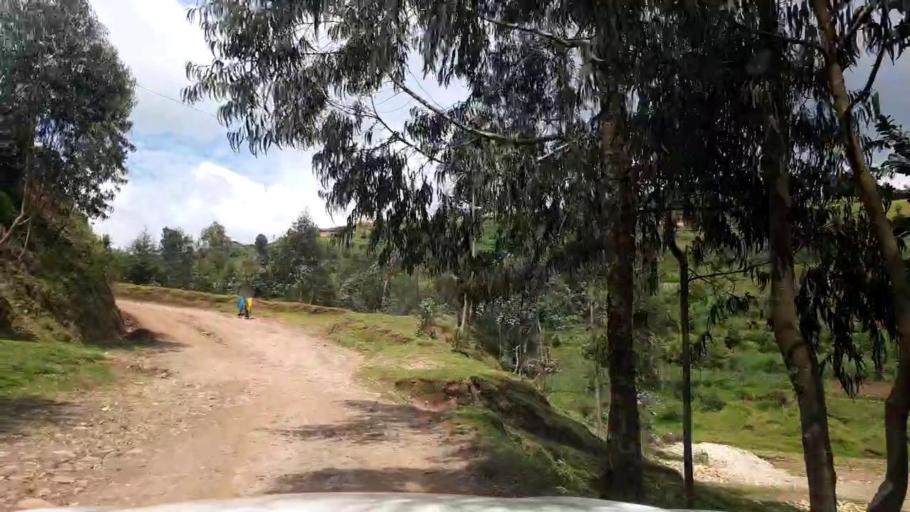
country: RW
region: Western Province
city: Kibuye
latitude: -1.9113
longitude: 29.4574
